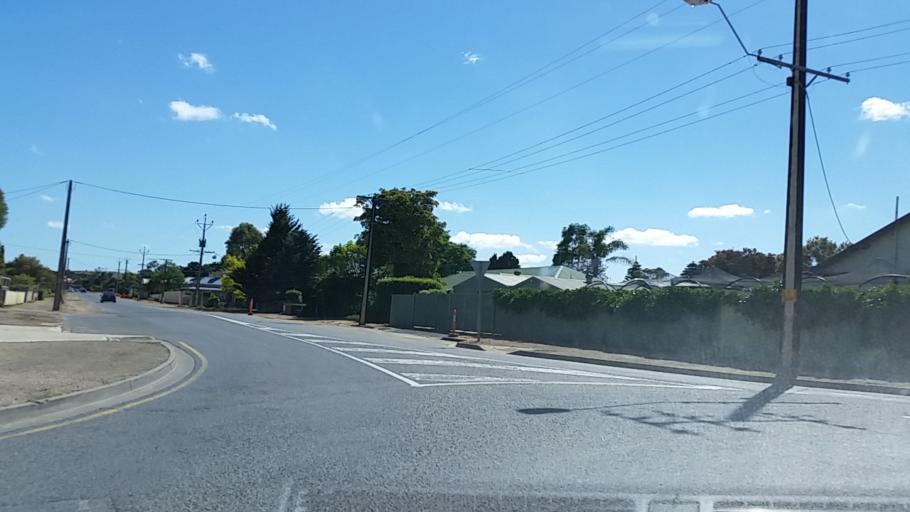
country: AU
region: South Australia
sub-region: Alexandrina
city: Strathalbyn
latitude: -35.2616
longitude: 138.8900
